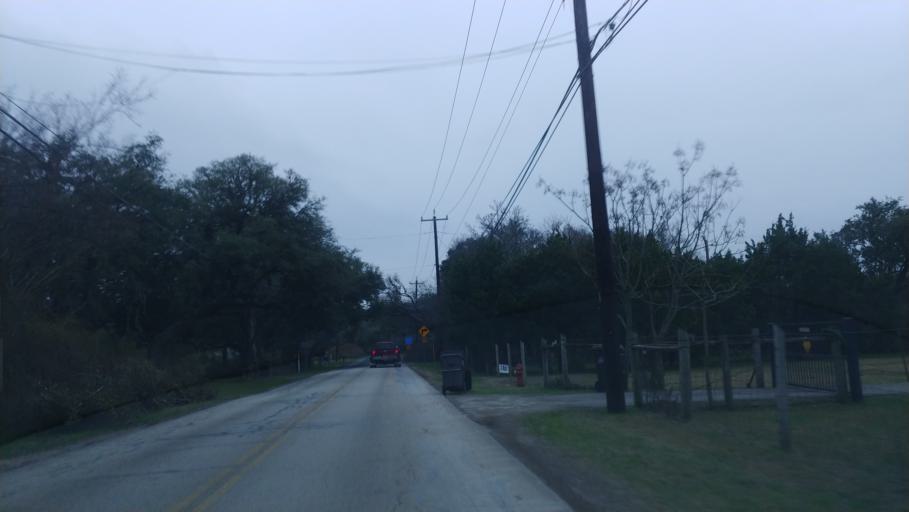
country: US
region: Texas
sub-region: Bexar County
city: Helotes
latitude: 29.6100
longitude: -98.6847
